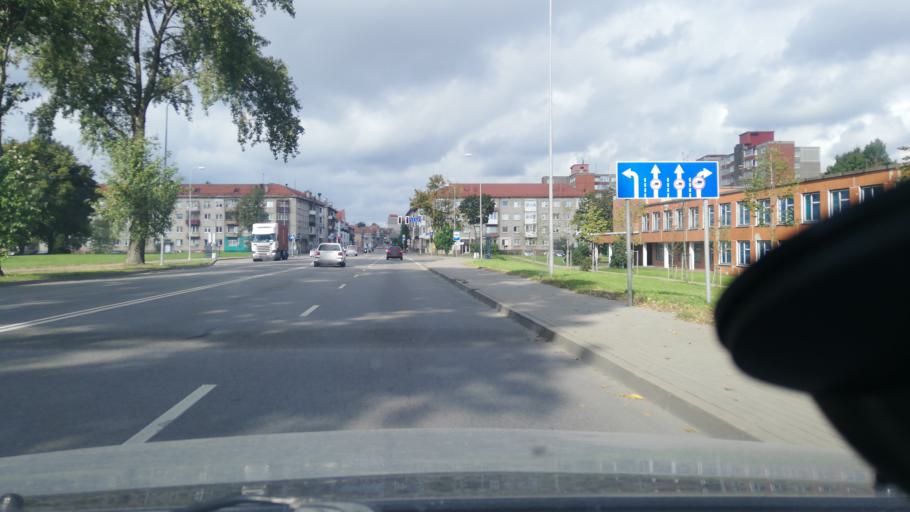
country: LT
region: Klaipedos apskritis
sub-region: Klaipeda
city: Klaipeda
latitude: 55.6747
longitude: 21.1555
